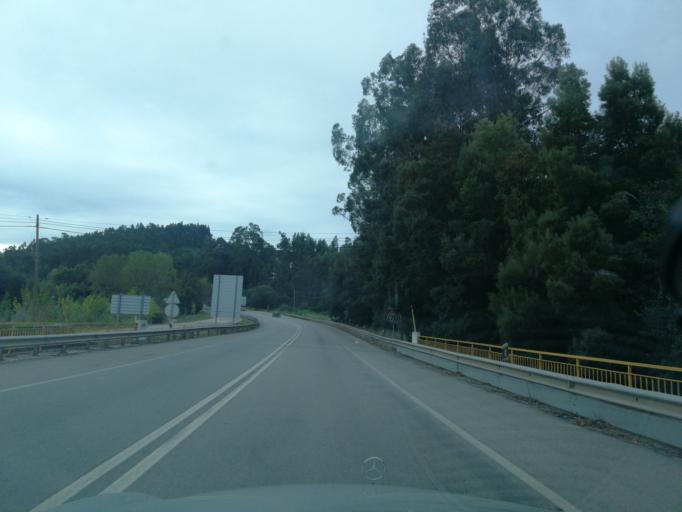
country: PT
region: Aveiro
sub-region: Agueda
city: Valongo
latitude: 40.6339
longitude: -8.4706
